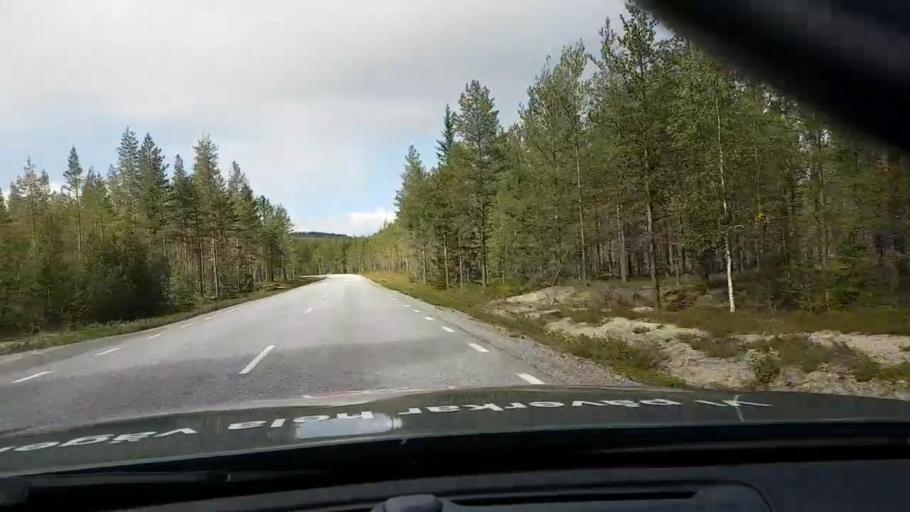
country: SE
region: Vaesternorrland
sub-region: OErnskoeldsviks Kommun
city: Bredbyn
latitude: 63.6832
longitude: 17.7798
